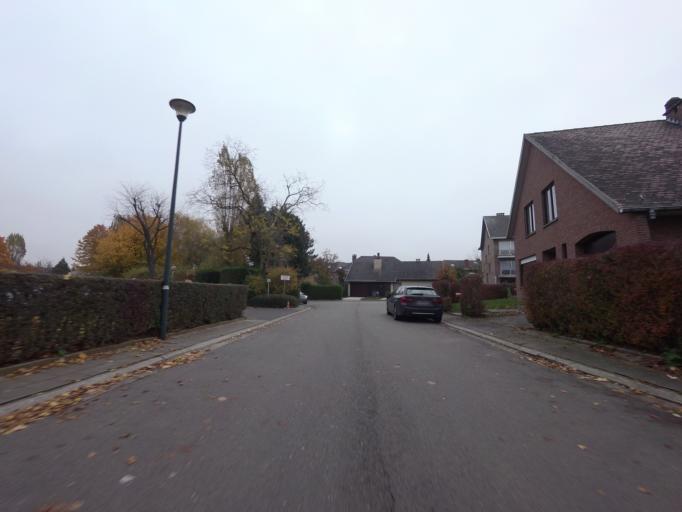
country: BE
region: Flanders
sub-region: Provincie Vlaams-Brabant
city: Diegem
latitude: 50.8669
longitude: 4.4338
